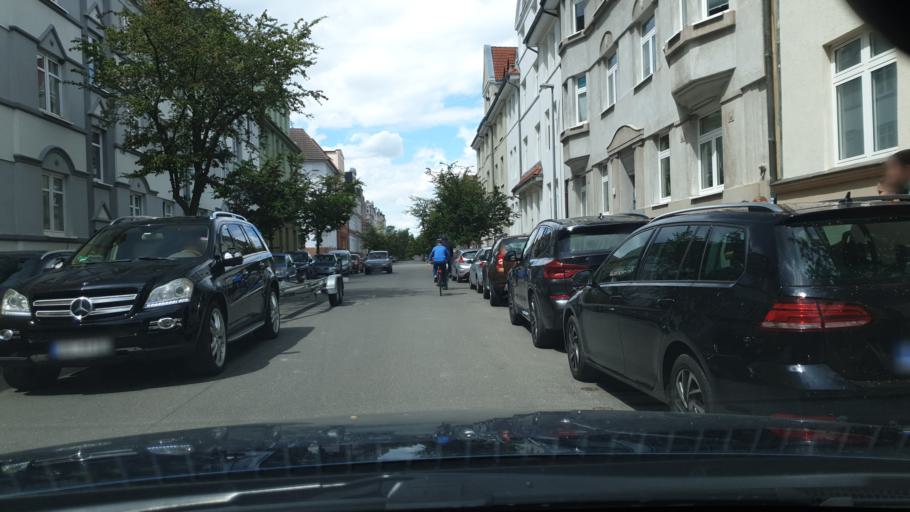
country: DE
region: Mecklenburg-Vorpommern
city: Werdervorstadt
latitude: 53.6365
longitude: 11.4273
